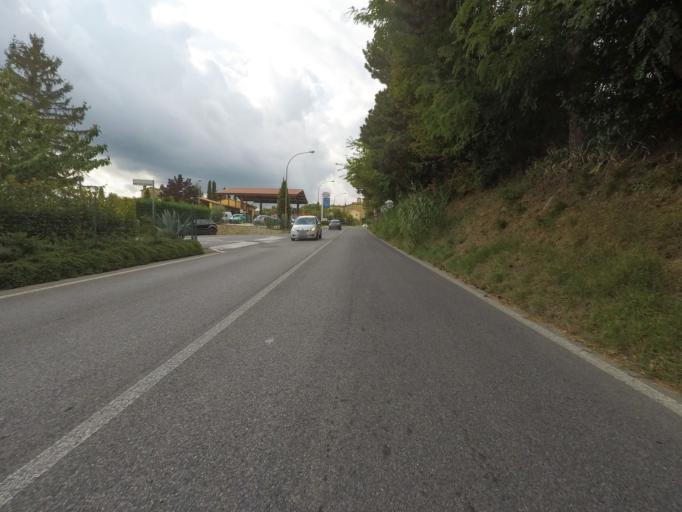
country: IT
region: Tuscany
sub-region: Provincia di Siena
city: Montepulciano
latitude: 43.1100
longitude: 11.7893
